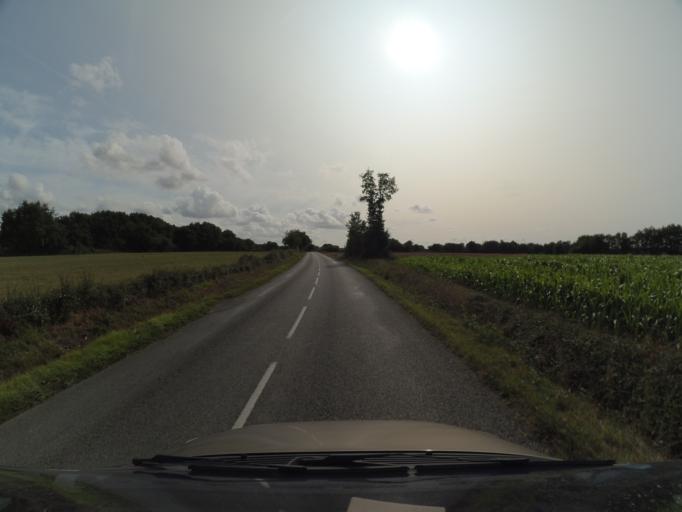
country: FR
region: Pays de la Loire
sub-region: Departement de la Vendee
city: Saint-Georges-de-Montaigu
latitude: 46.9554
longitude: -1.2862
